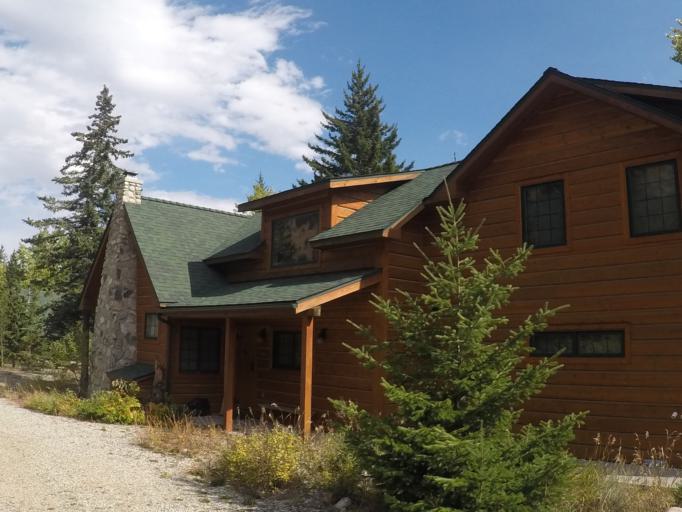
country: US
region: Montana
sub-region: Carbon County
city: Red Lodge
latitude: 45.0933
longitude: -109.3172
